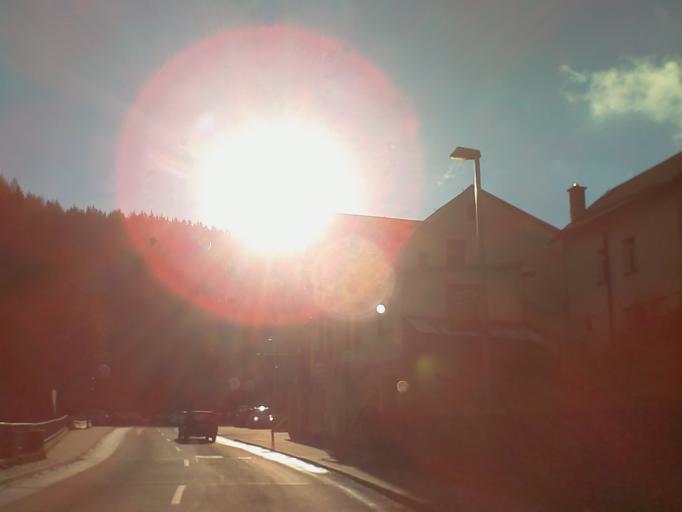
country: DE
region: Thuringia
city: Katzhutte
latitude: 50.5518
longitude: 11.0524
